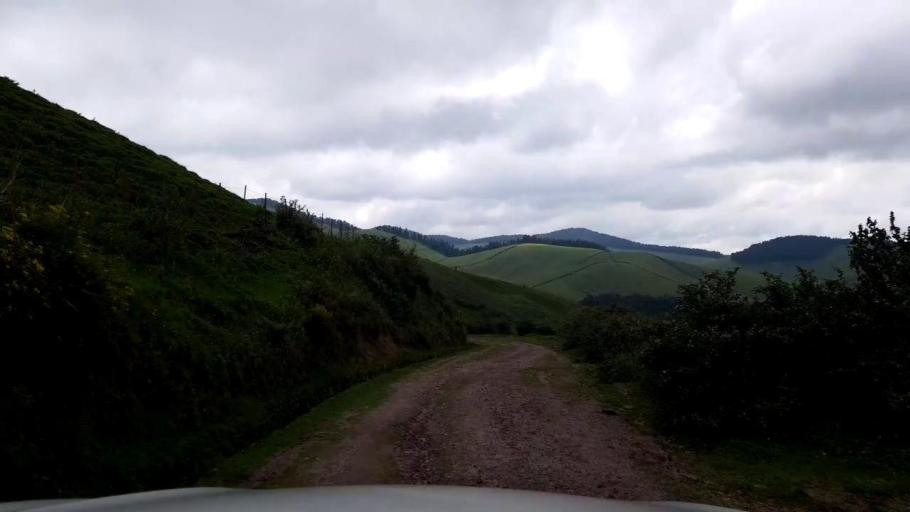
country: RW
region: Western Province
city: Gisenyi
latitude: -1.6780
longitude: 29.4175
